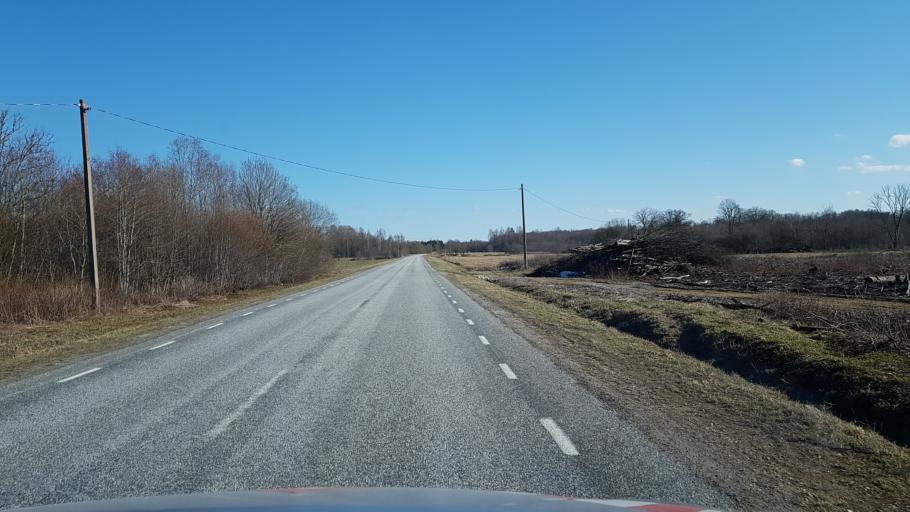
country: EE
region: Laeaene-Virumaa
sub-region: Haljala vald
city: Haljala
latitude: 59.4883
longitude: 26.1483
